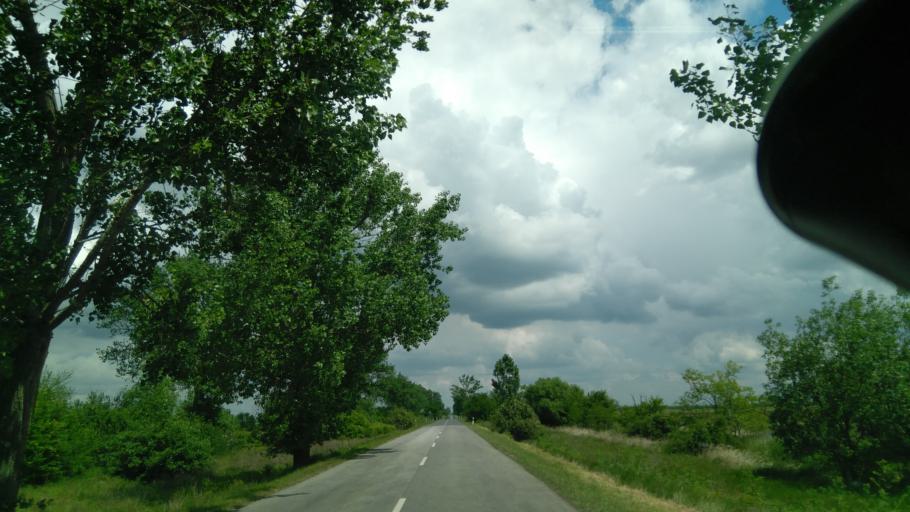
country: HU
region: Bekes
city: Devavanya
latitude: 47.0038
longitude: 20.9162
